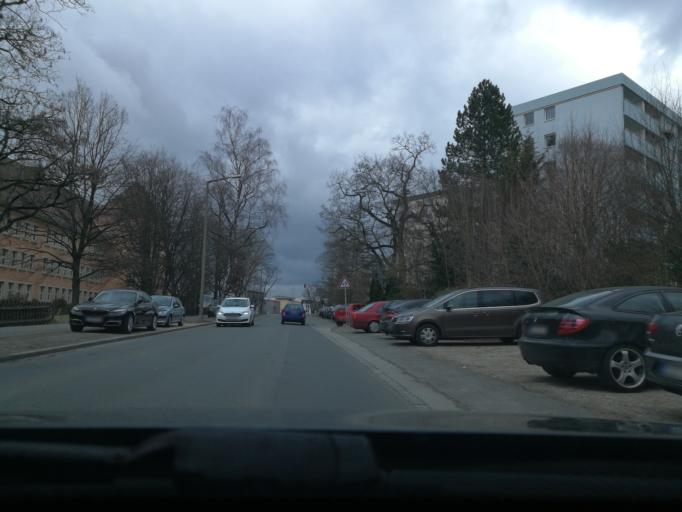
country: DE
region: Bavaria
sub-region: Regierungsbezirk Mittelfranken
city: Nuernberg
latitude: 49.4712
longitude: 11.1155
